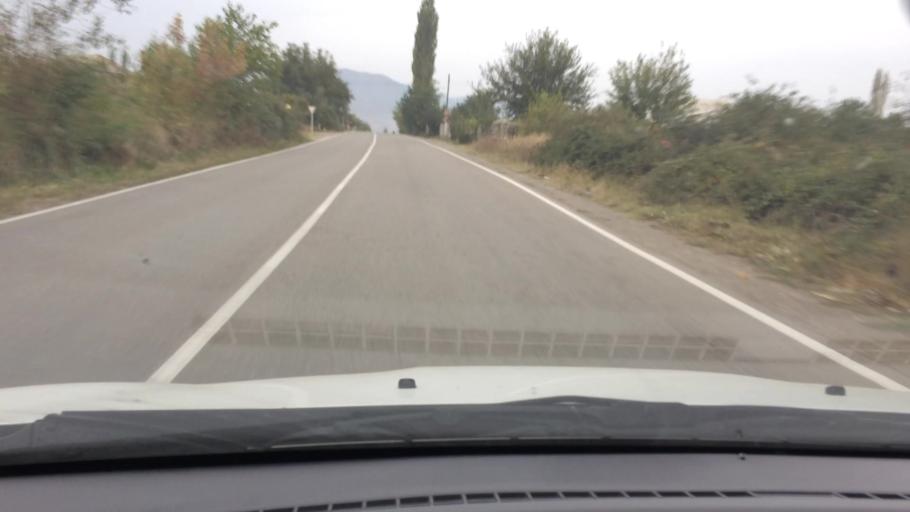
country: AM
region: Tavush
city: Bagratashen
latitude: 41.2355
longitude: 44.8086
